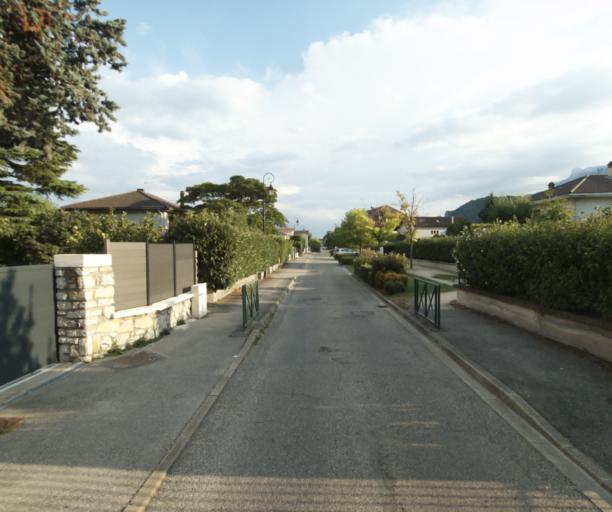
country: FR
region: Rhone-Alpes
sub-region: Departement de l'Isere
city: Seyssinet-Pariset
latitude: 45.1650
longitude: 5.6967
